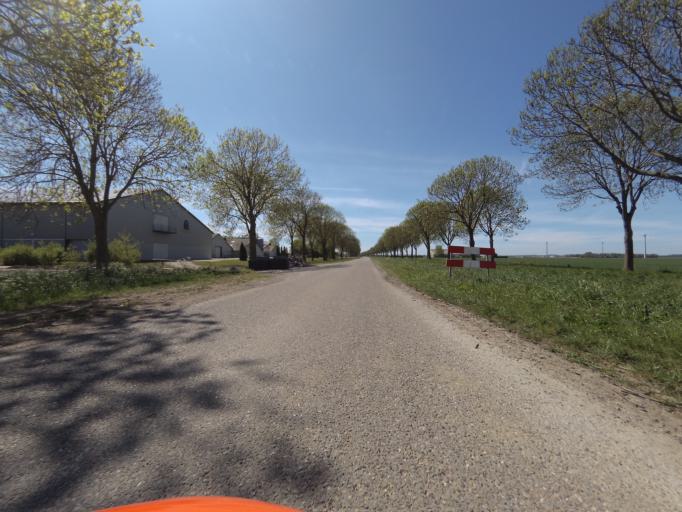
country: NL
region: Utrecht
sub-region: Gemeente Bunschoten
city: Spakenburg
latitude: 52.3254
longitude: 5.3951
